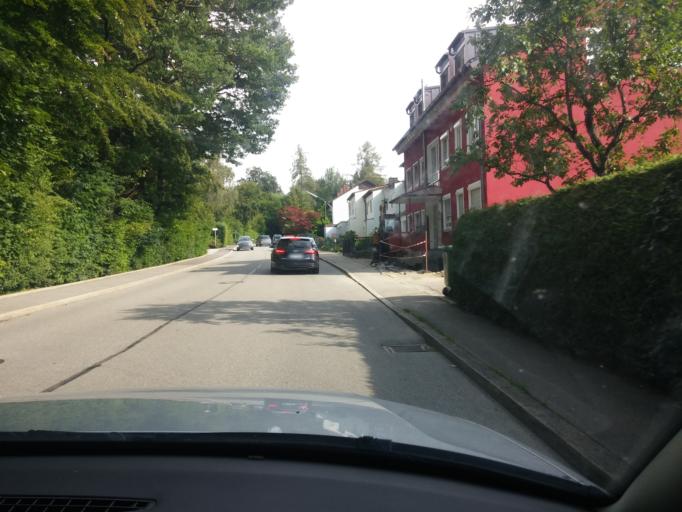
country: DE
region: Bavaria
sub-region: Upper Bavaria
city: Kirchseeon
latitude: 48.0650
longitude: 11.8919
